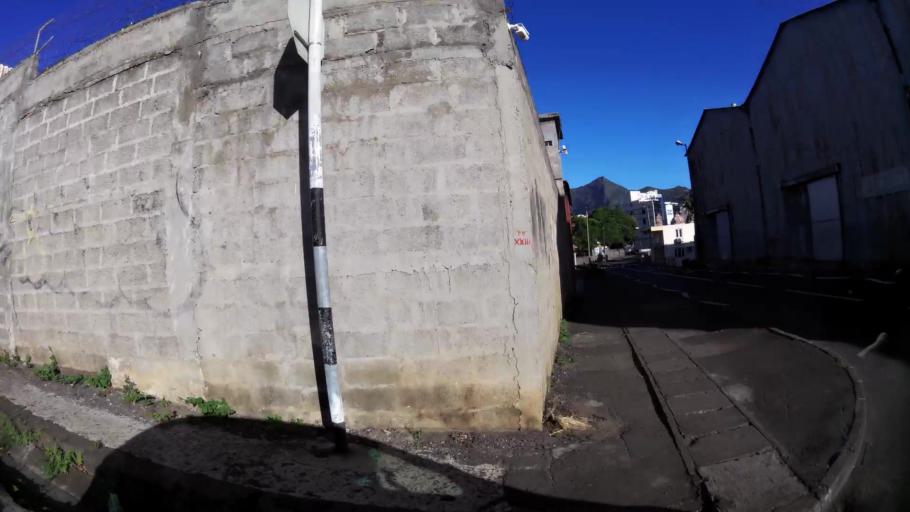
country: MU
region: Port Louis
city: Port Louis
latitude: -20.1555
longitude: 57.5059
